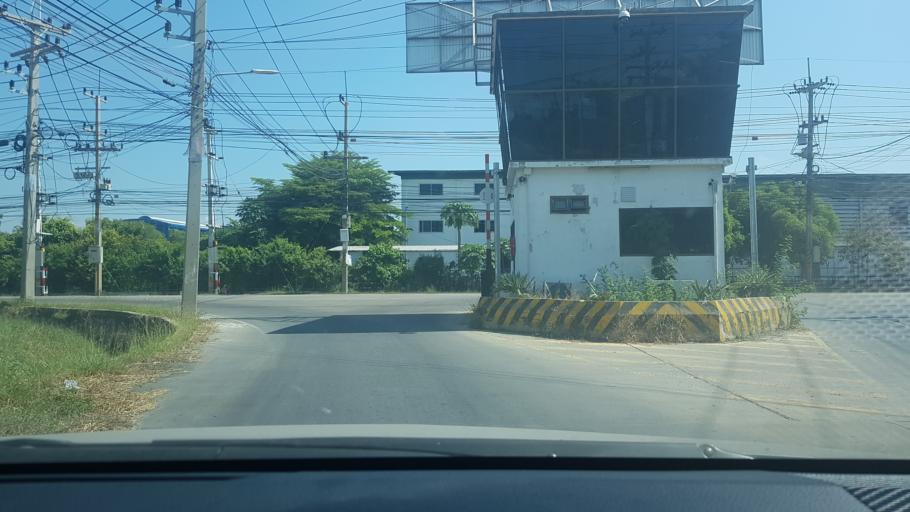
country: TH
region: Phra Nakhon Si Ayutthaya
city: Bang Pa-in
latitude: 14.2474
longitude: 100.5998
